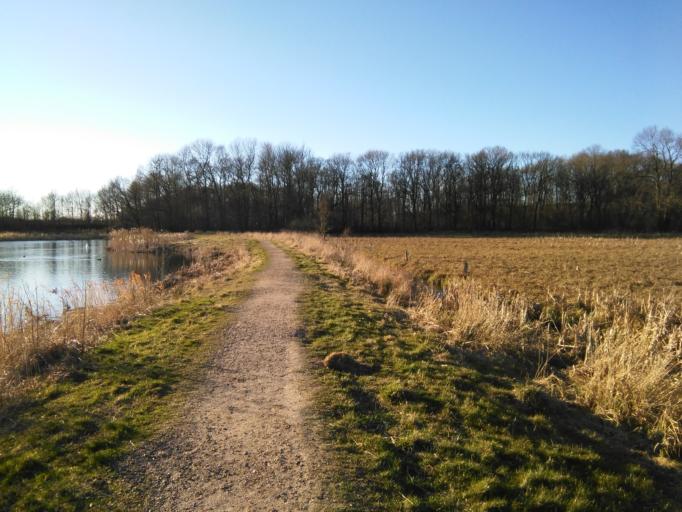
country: DK
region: Central Jutland
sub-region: Arhus Kommune
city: Malling
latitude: 56.0459
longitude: 10.2019
